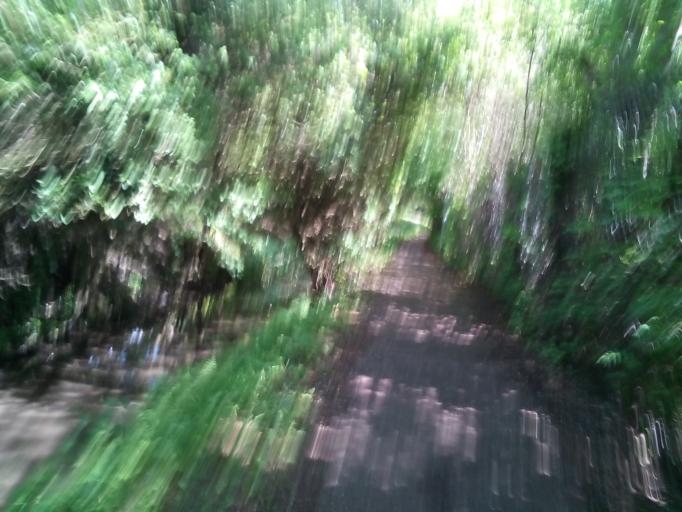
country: GB
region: England
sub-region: Cambridgeshire
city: Cambridge
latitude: 52.1929
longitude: 0.1619
